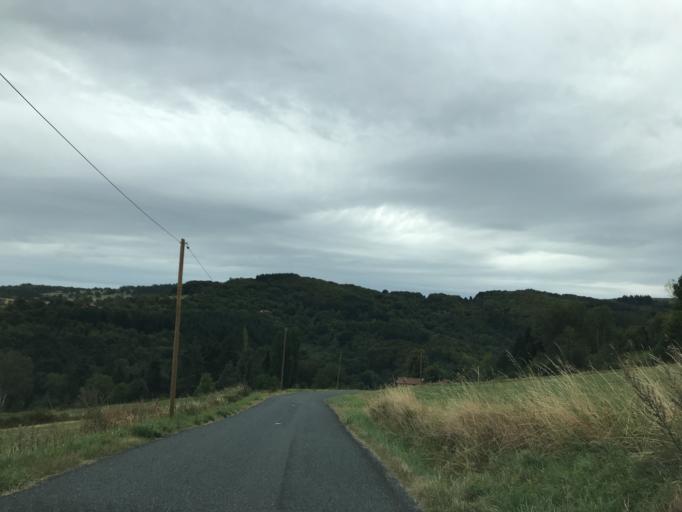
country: FR
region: Rhone-Alpes
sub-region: Departement de la Loire
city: Sail-sous-Couzan
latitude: 45.6816
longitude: 3.9091
